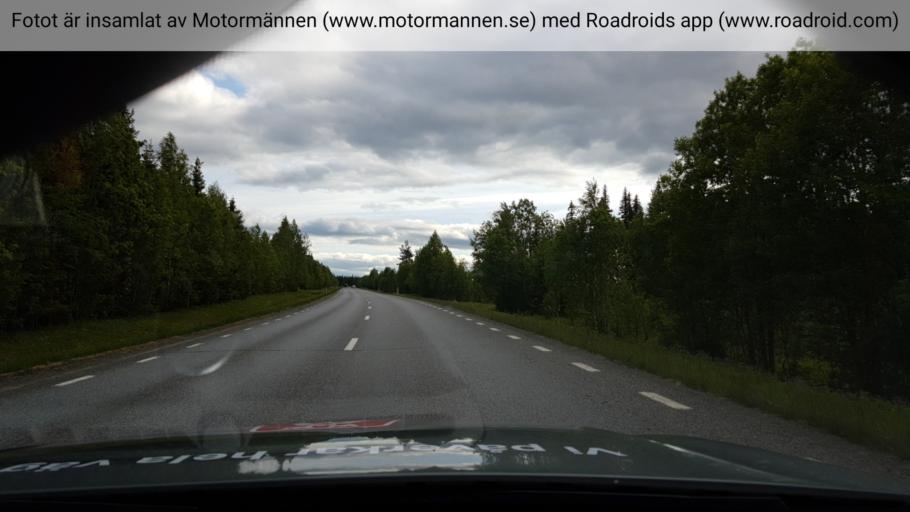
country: SE
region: Jaemtland
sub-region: Stroemsunds Kommun
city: Stroemsund
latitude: 63.5170
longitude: 15.2923
